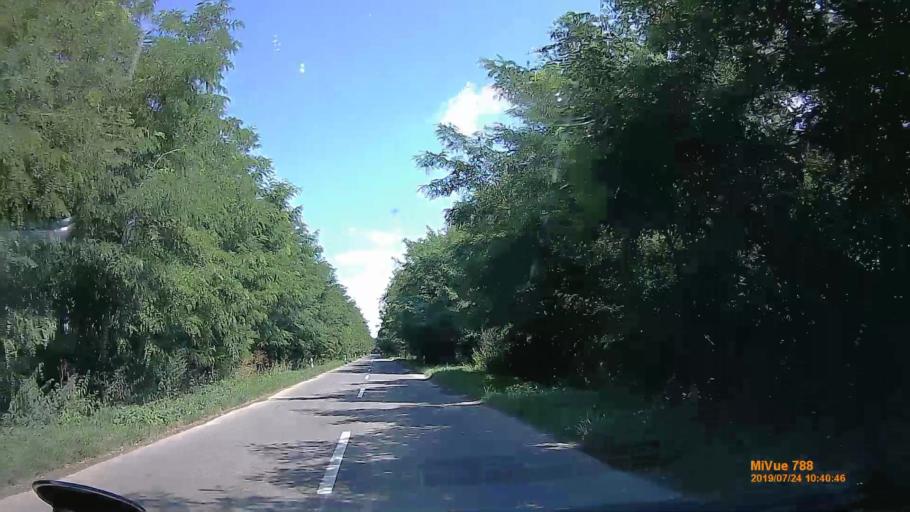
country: HU
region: Szabolcs-Szatmar-Bereg
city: Tarpa
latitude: 48.1793
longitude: 22.5473
